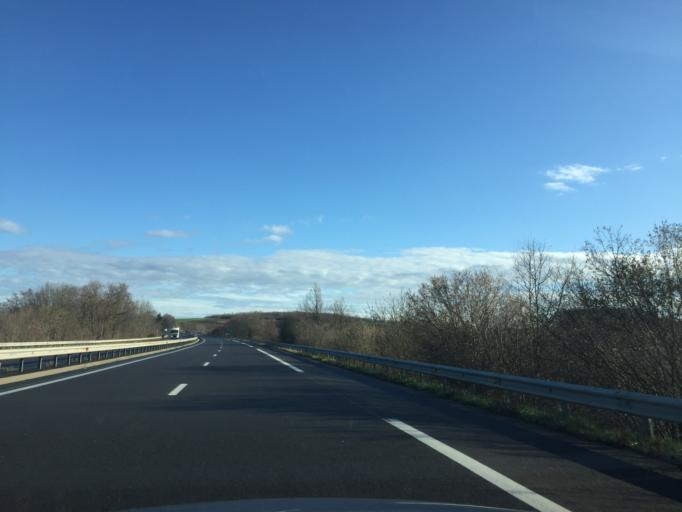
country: FR
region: Auvergne
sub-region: Departement du Puy-de-Dome
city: Culhat
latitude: 45.8400
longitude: 3.3261
